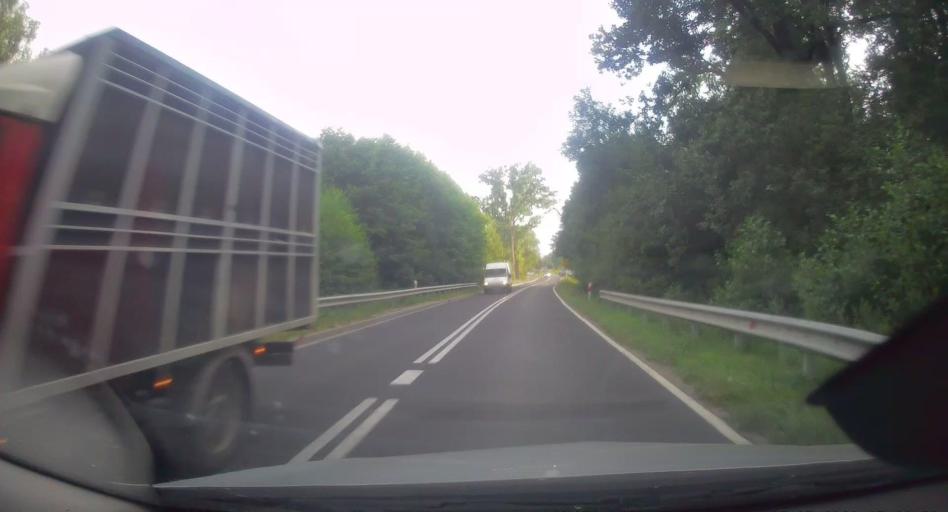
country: PL
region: Lesser Poland Voivodeship
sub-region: Powiat brzeski
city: Przyborow
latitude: 50.0359
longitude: 20.6446
